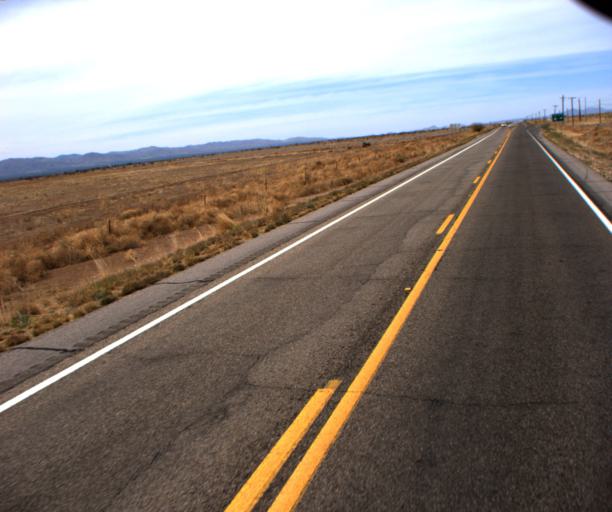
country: US
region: Arizona
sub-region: Cochise County
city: Pirtleville
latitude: 31.4436
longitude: -109.5982
